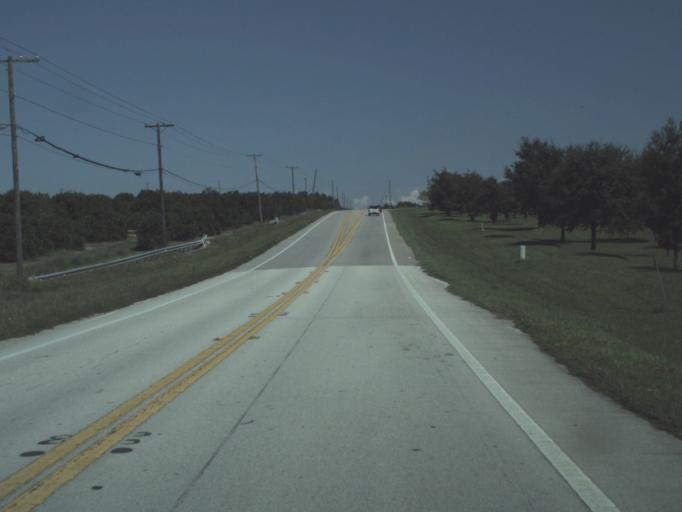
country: US
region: Florida
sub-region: Polk County
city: Lake Hamilton
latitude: 28.0705
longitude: -81.6200
